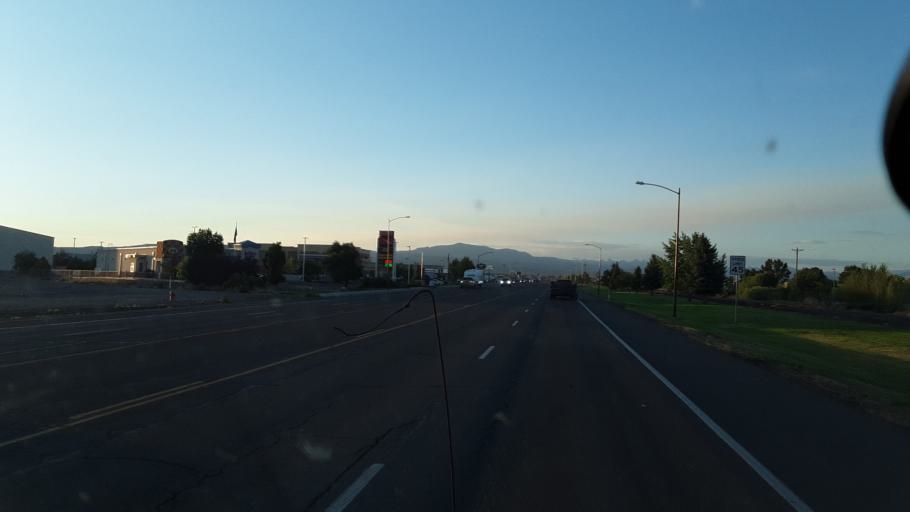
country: US
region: Colorado
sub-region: Montrose County
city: Montrose
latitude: 38.4994
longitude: -107.9000
